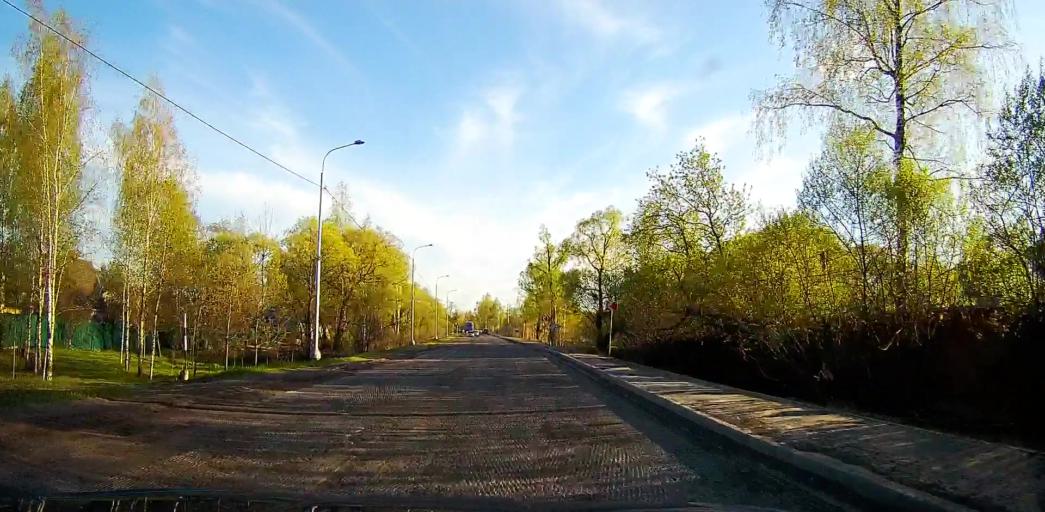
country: RU
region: Moskovskaya
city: Bronnitsy
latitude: 55.3040
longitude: 38.2112
